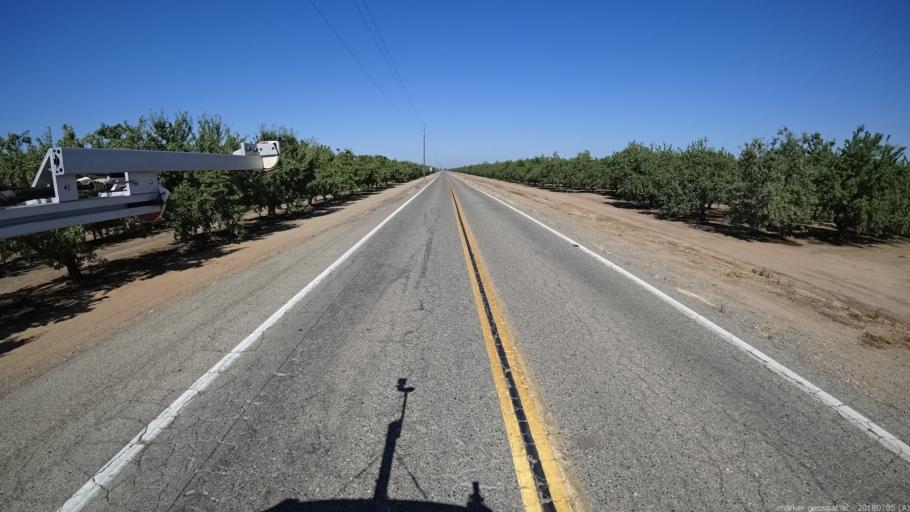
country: US
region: California
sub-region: Madera County
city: Fairmead
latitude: 37.1271
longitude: -120.1518
